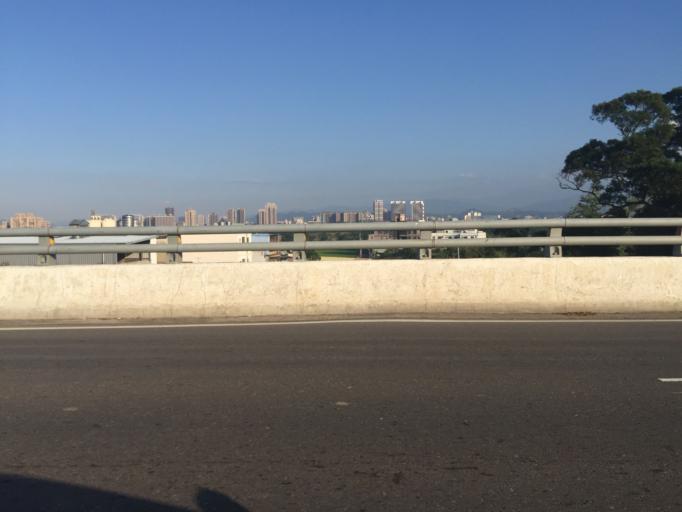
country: TW
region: Taiwan
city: Daxi
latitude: 24.9310
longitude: 121.2605
